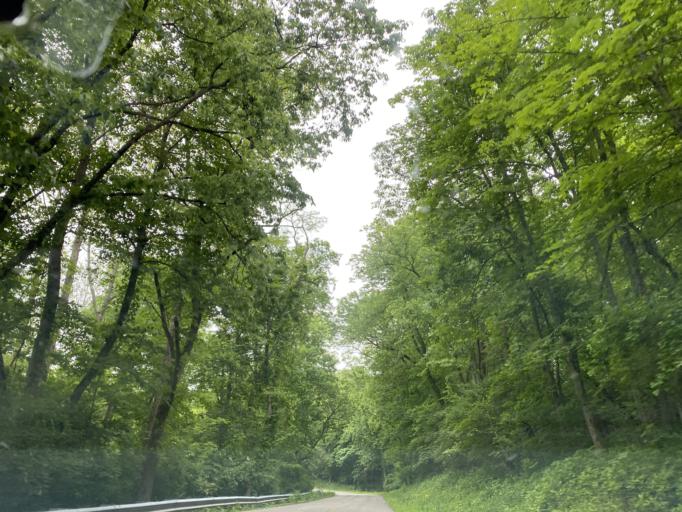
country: US
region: Kentucky
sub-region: Campbell County
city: Dayton
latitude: 39.1021
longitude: -84.4622
